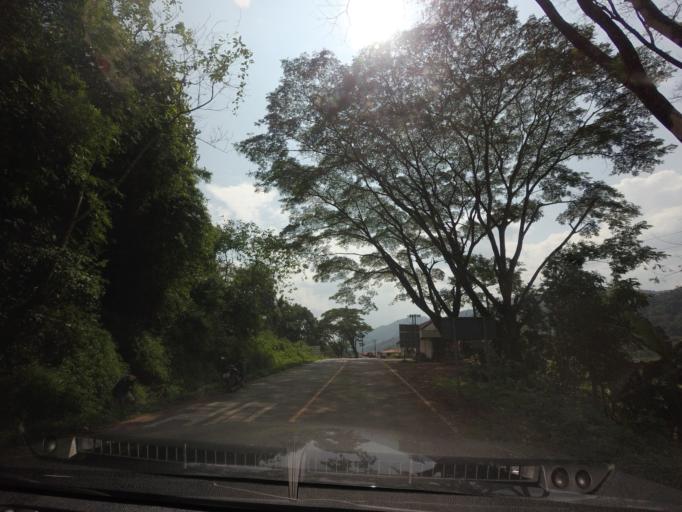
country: TH
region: Nan
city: Bo Kluea
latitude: 19.1534
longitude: 101.1580
